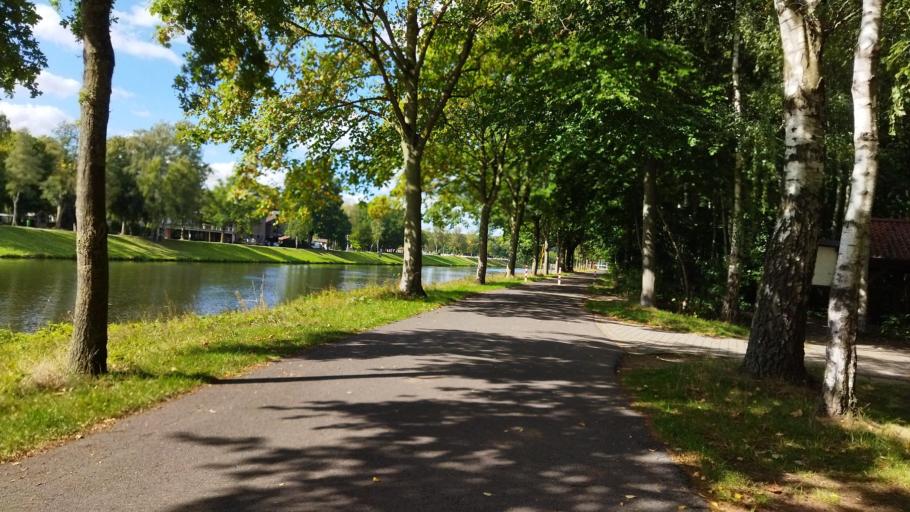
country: DE
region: Lower Saxony
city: Lingen
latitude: 52.4699
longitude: 7.3089
